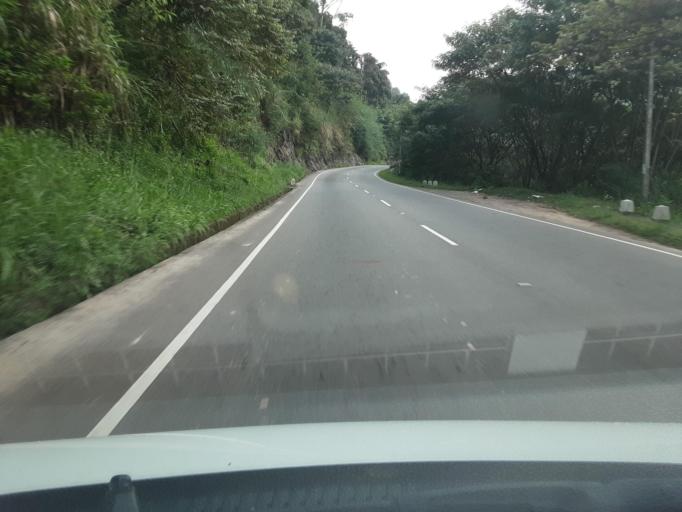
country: LK
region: Uva
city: Badulla
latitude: 6.9498
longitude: 81.0187
